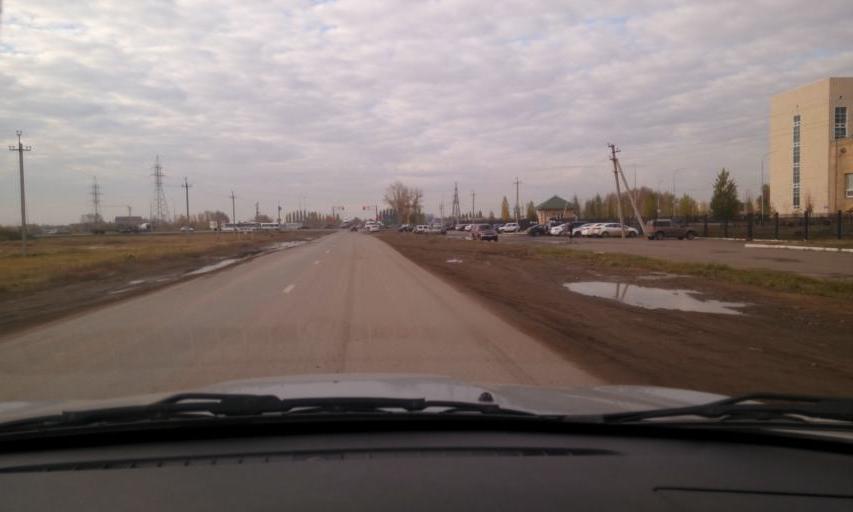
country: KZ
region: Astana Qalasy
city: Astana
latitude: 51.1403
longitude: 71.5303
